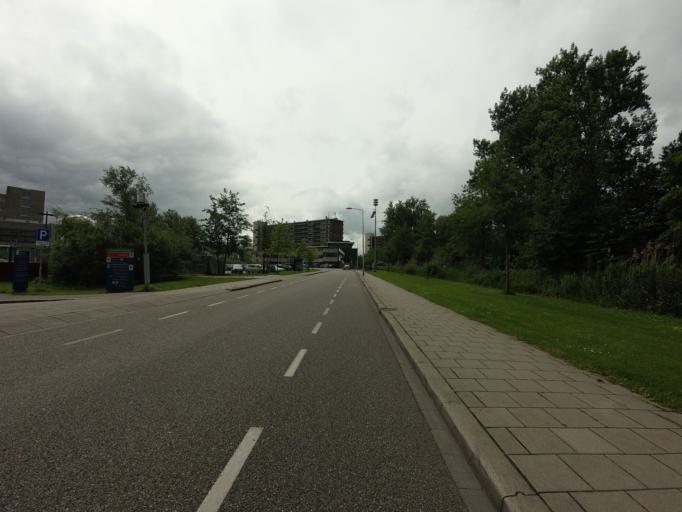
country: NL
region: South Holland
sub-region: Gemeente Gouda
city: Gouda
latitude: 52.0224
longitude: 4.7050
